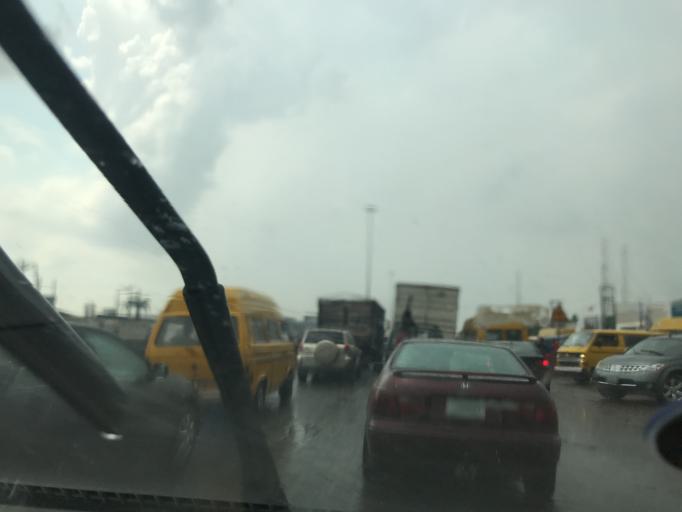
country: NG
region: Lagos
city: Oshodi
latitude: 6.5528
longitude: 3.3447
